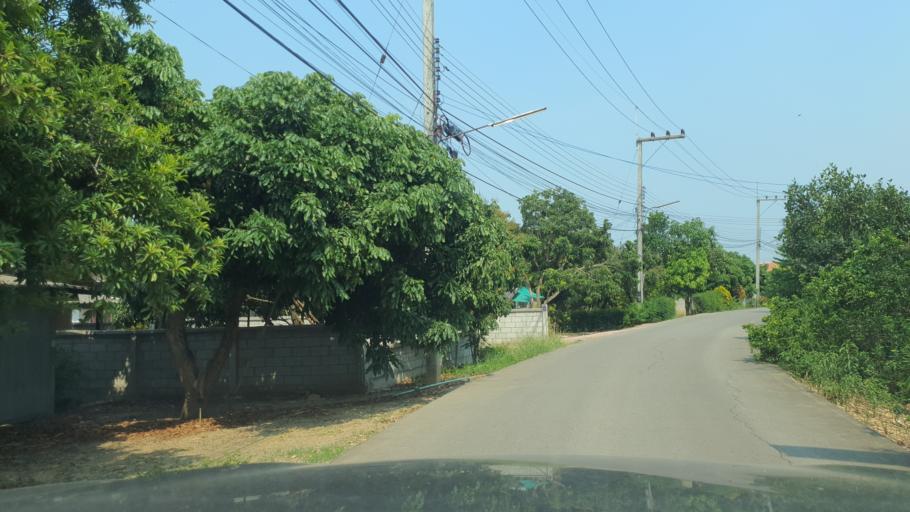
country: TH
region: Lamphun
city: Lamphun
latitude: 18.6400
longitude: 98.9917
